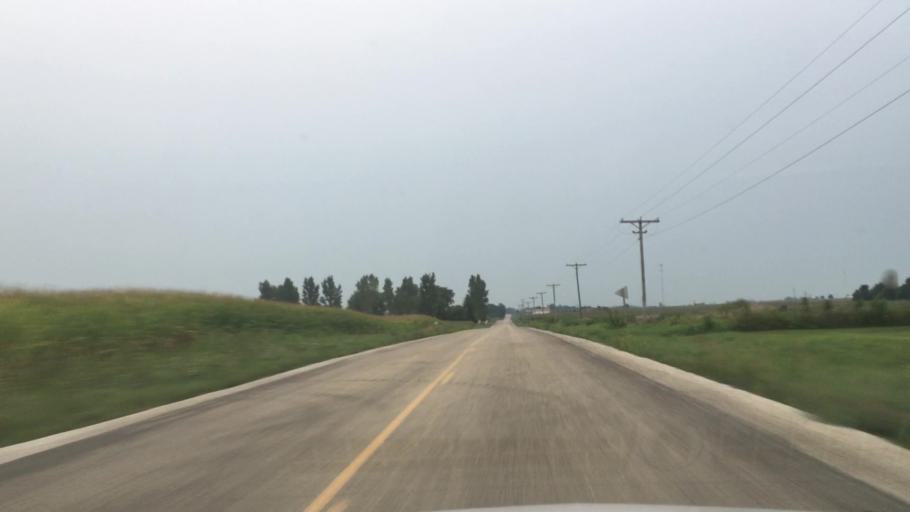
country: US
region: Illinois
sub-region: DeKalb County
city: Waterman
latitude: 41.8239
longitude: -88.7733
